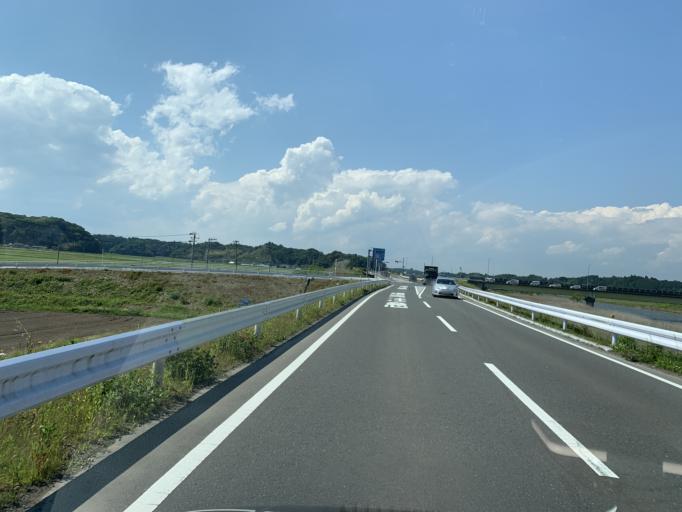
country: JP
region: Miyagi
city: Yamoto
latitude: 38.3938
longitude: 141.1565
